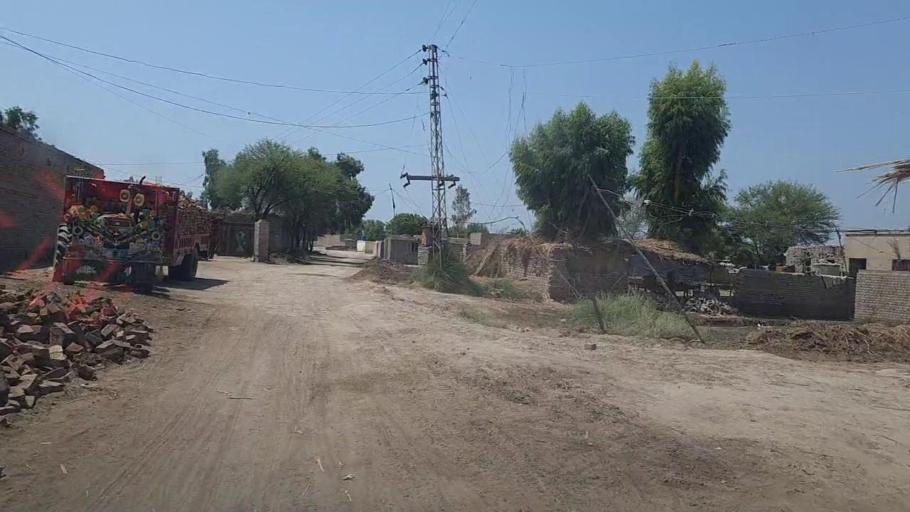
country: PK
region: Sindh
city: Ubauro
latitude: 28.1940
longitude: 69.8003
